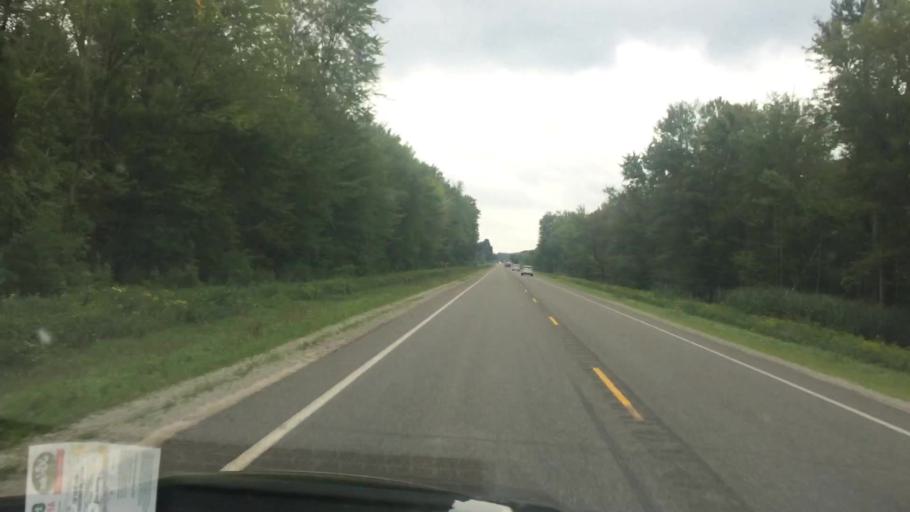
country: US
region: Michigan
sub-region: Tuscola County
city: Cass City
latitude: 43.6236
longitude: -83.0971
